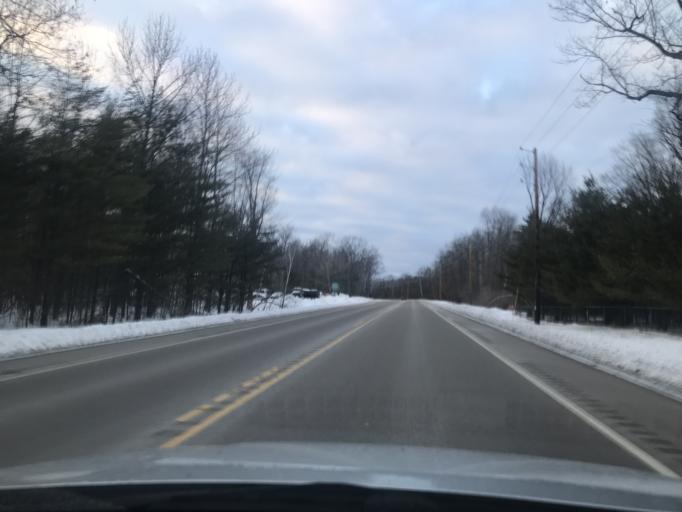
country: US
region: Wisconsin
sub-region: Marinette County
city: Marinette
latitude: 45.1511
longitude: -87.7049
